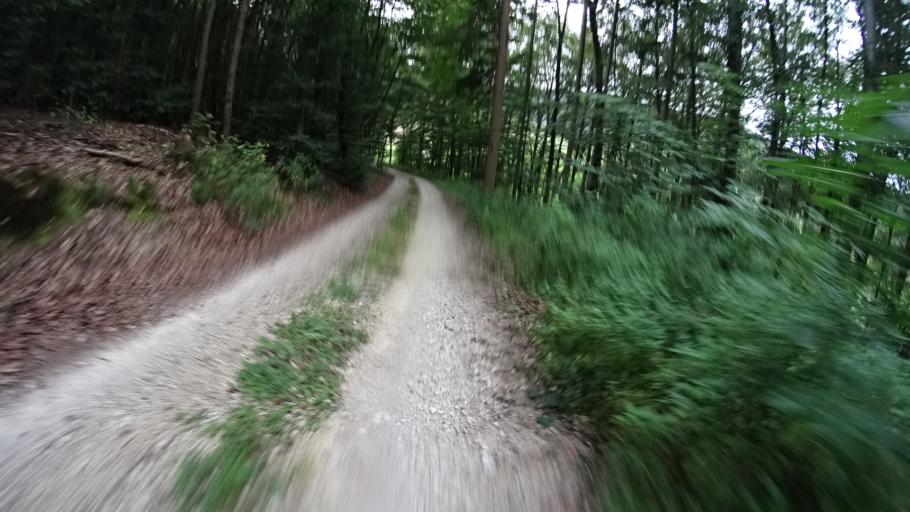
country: DE
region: Bavaria
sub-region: Upper Bavaria
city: Walting
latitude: 48.9014
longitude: 11.2963
